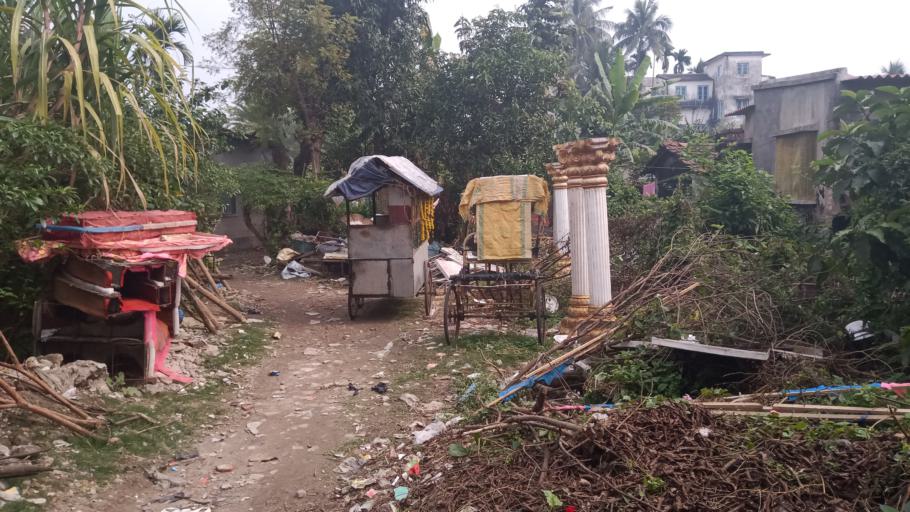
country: IN
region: West Bengal
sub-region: Kolkata
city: Kolkata
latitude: 22.4656
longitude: 88.3829
